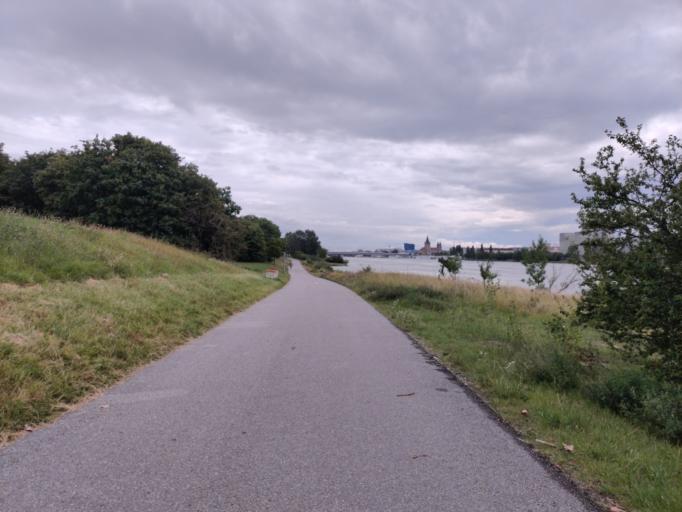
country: AT
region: Vienna
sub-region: Wien Stadt
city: Vienna
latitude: 48.2382
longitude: 16.3964
